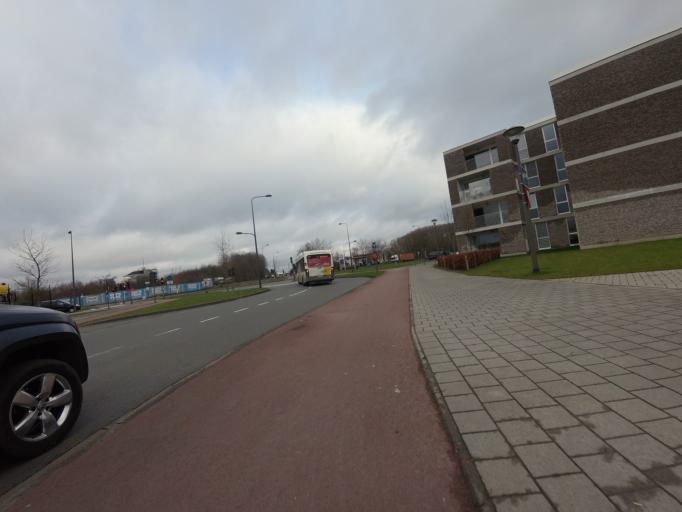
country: BE
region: Flanders
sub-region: Provincie Antwerpen
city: Hoboken
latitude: 51.1915
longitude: 4.3695
